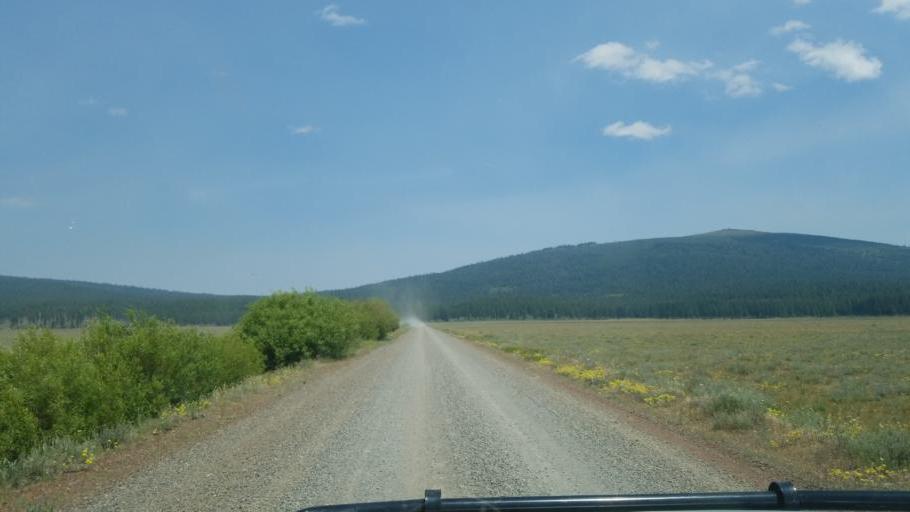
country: US
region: California
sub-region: Lassen County
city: Westwood
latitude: 40.5914
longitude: -120.9730
